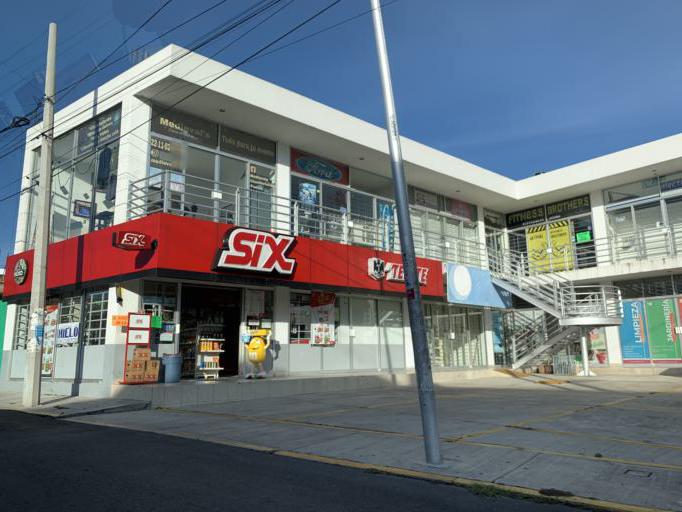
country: MX
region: Puebla
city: Puebla
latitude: 19.0149
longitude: -98.2282
